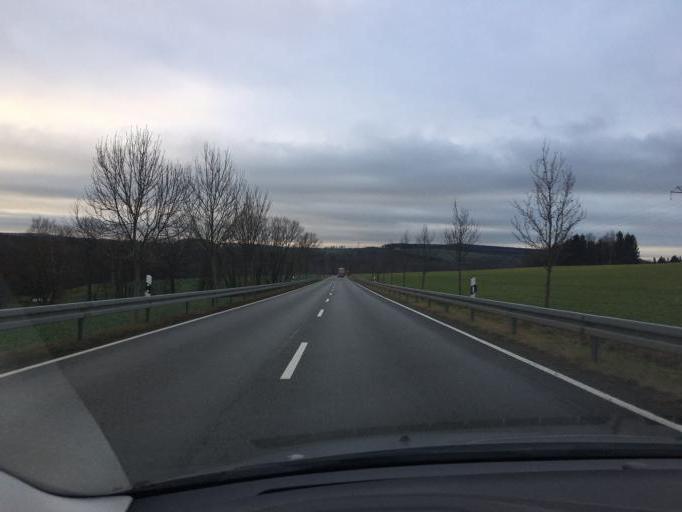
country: DE
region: Thuringia
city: Juckelberg
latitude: 50.9069
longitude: 12.6478
